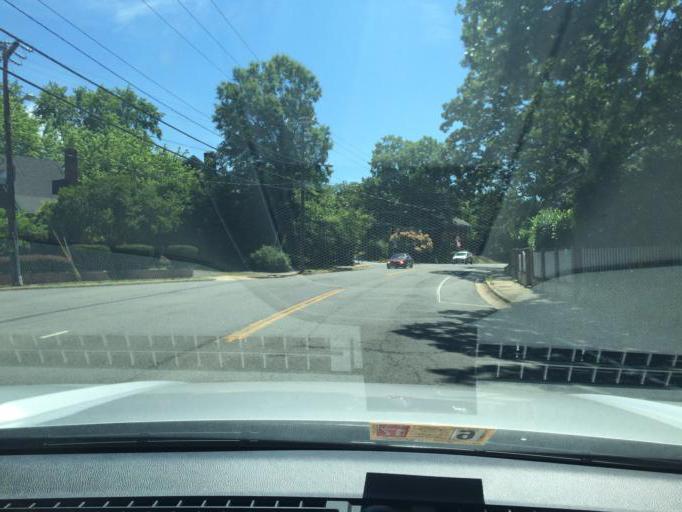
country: US
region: Virginia
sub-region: Fairfax County
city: Huntington
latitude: 38.8249
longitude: -77.0756
